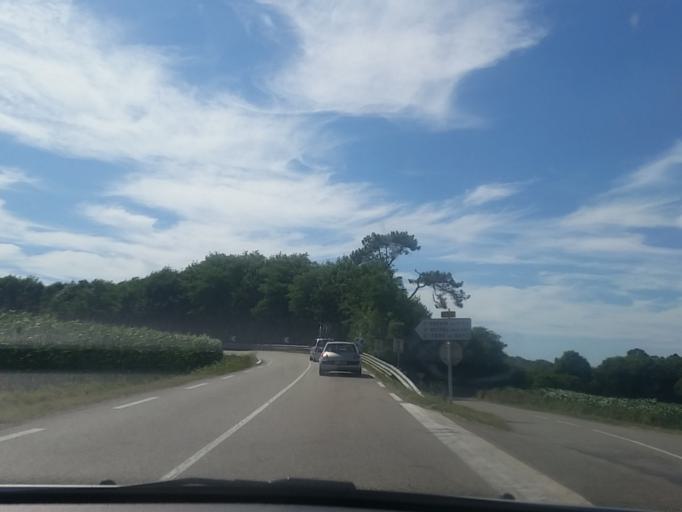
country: FR
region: Pays de la Loire
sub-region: Departement de la Loire-Atlantique
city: Chauve
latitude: 47.1880
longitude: -1.9544
